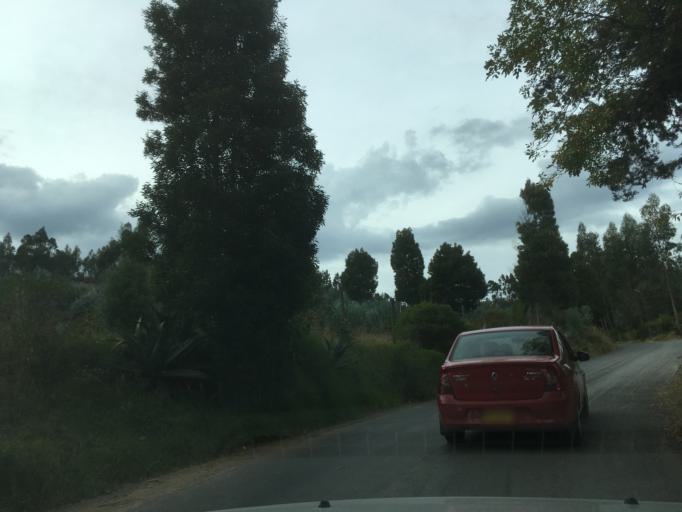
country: CO
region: Boyaca
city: Firavitoba
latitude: 5.6786
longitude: -73.0054
